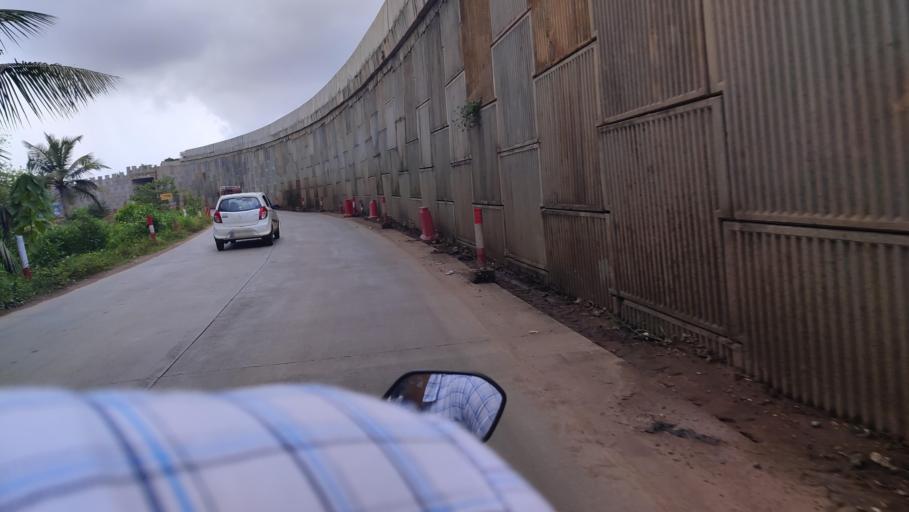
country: IN
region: Kerala
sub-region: Kasaragod District
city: Nileshwar
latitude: 12.2421
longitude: 75.1482
